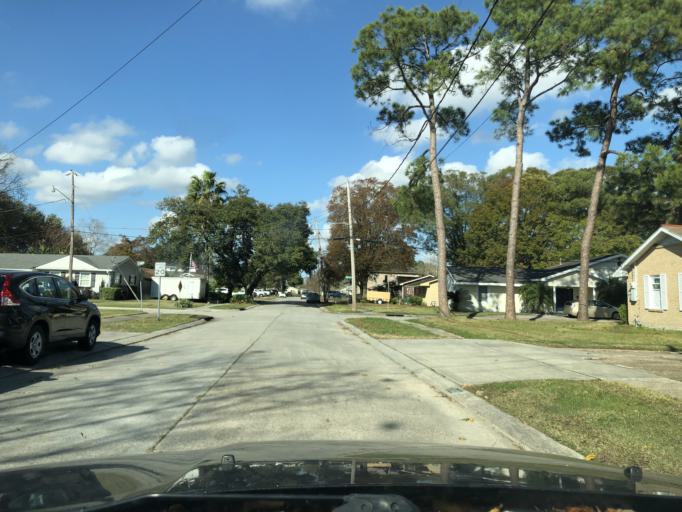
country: US
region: Louisiana
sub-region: Jefferson Parish
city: Metairie Terrace
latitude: 29.9833
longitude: -90.1652
